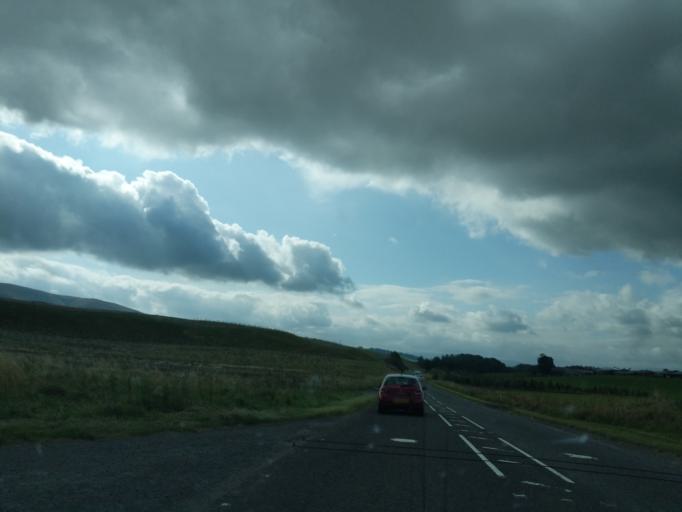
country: GB
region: Scotland
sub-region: Midlothian
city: Penicuik
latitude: 55.7597
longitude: -3.2071
